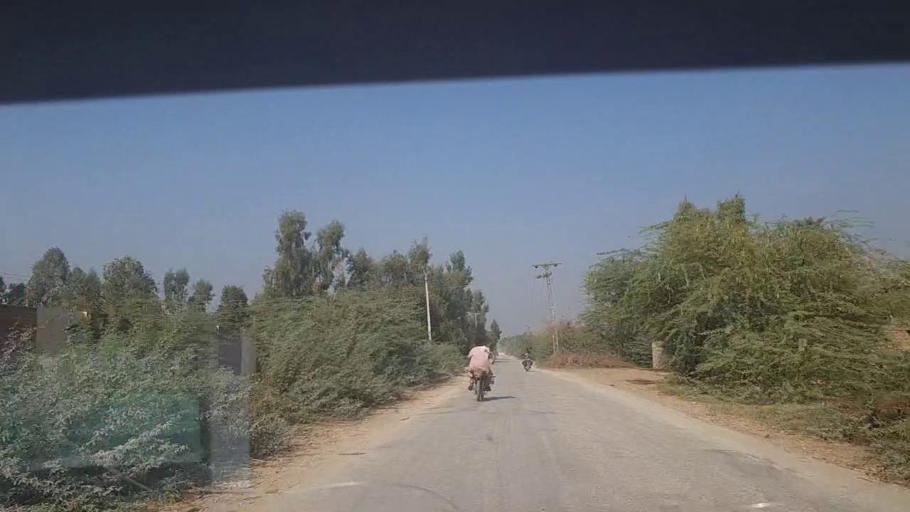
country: PK
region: Sindh
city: Kot Diji
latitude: 27.3537
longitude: 68.7113
